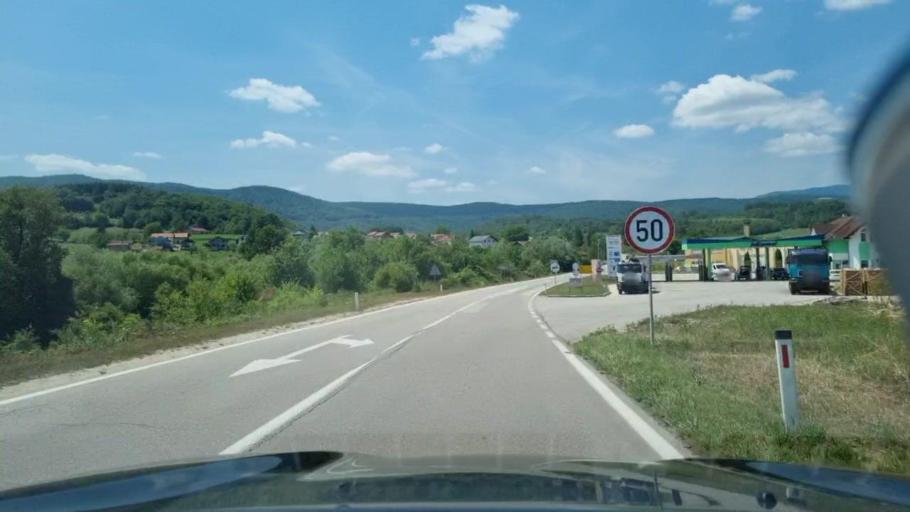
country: BA
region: Federation of Bosnia and Herzegovina
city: Velagici
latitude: 44.5595
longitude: 16.7170
